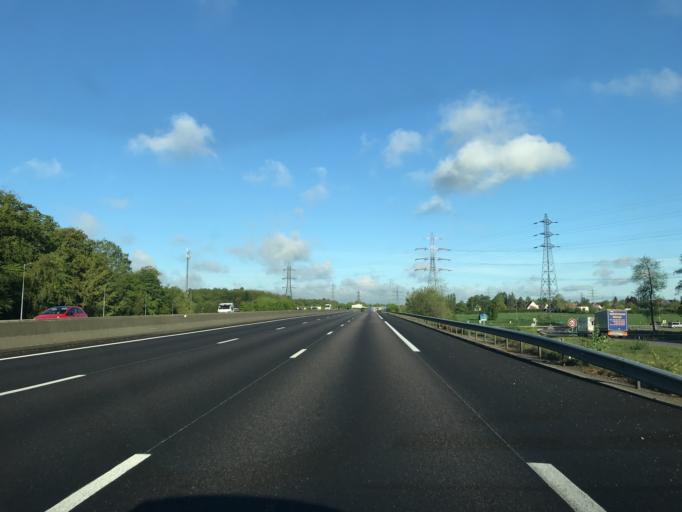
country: FR
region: Haute-Normandie
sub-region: Departement de la Seine-Maritime
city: Sahurs
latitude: 49.3417
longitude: 0.9327
